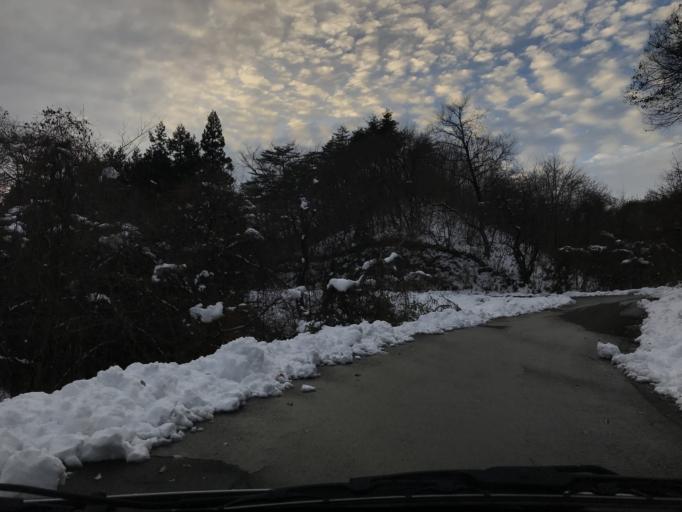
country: JP
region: Iwate
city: Mizusawa
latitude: 39.0411
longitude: 141.0311
